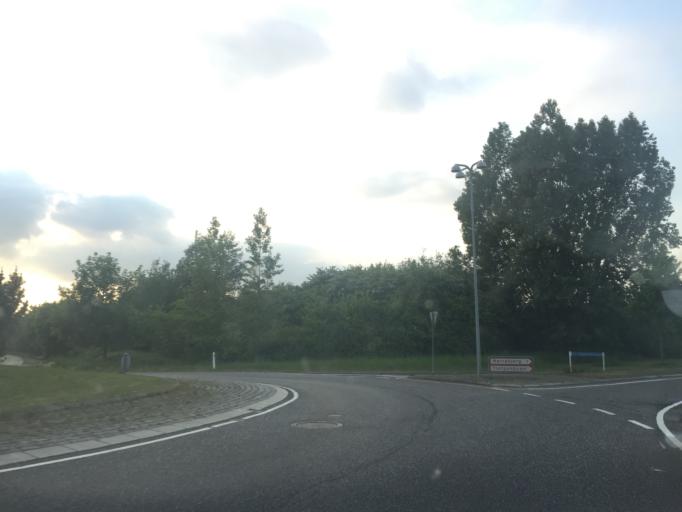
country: DK
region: South Denmark
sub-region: Odense Kommune
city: Neder Holluf
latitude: 55.3588
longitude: 10.4749
